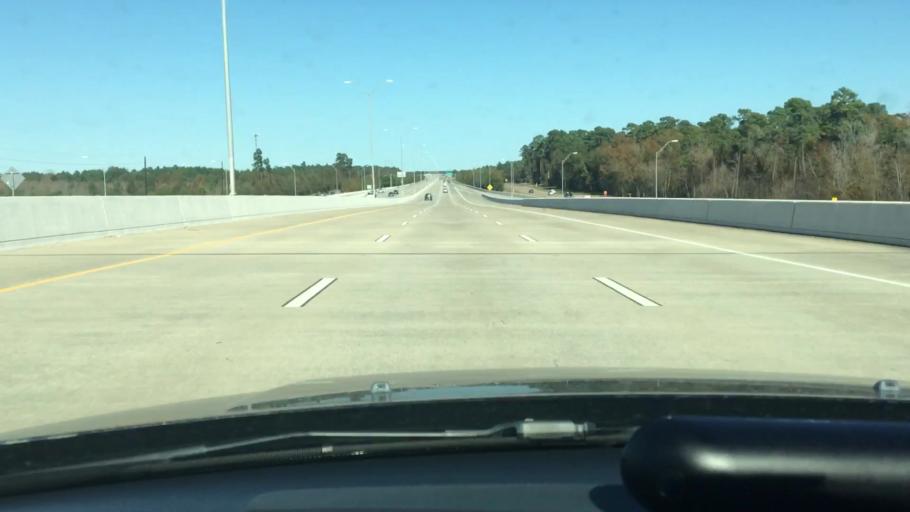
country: US
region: Texas
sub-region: Harris County
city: Sheldon
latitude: 29.8547
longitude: -95.1869
